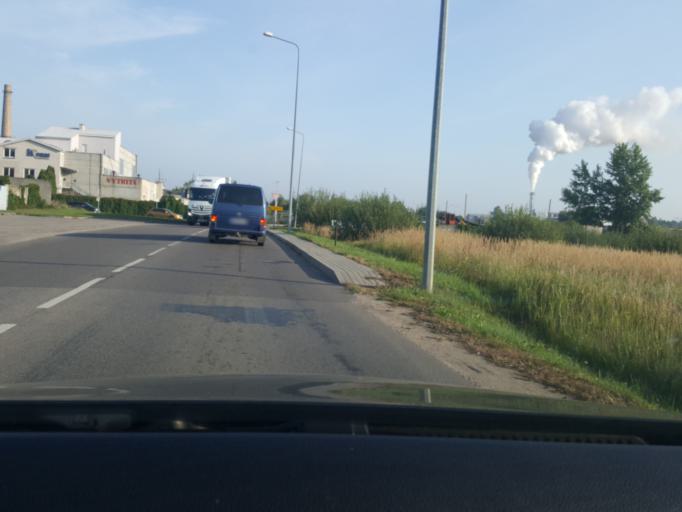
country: LT
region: Alytaus apskritis
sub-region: Alytus
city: Alytus
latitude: 54.4365
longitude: 24.0179
